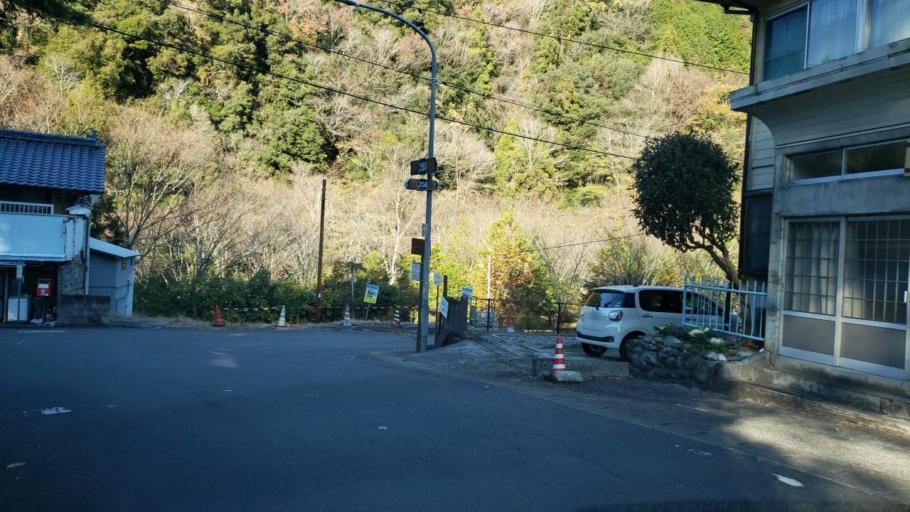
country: JP
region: Tokushima
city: Wakimachi
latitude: 34.0026
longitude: 134.0378
